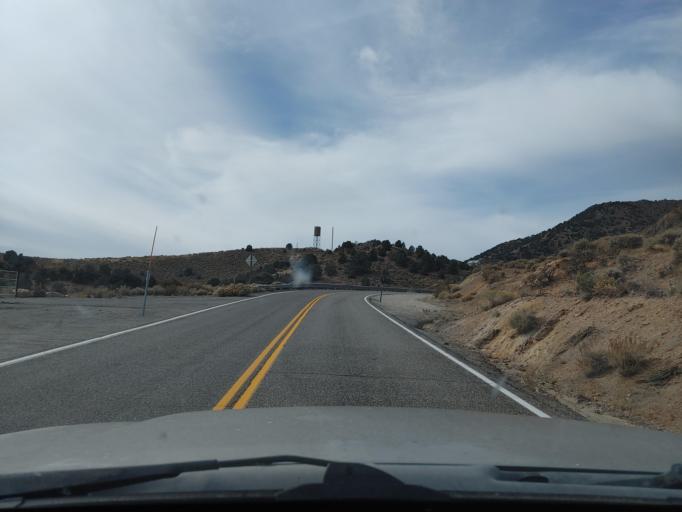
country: US
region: Nevada
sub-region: Storey County
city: Virginia City
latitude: 39.2973
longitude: -119.6469
